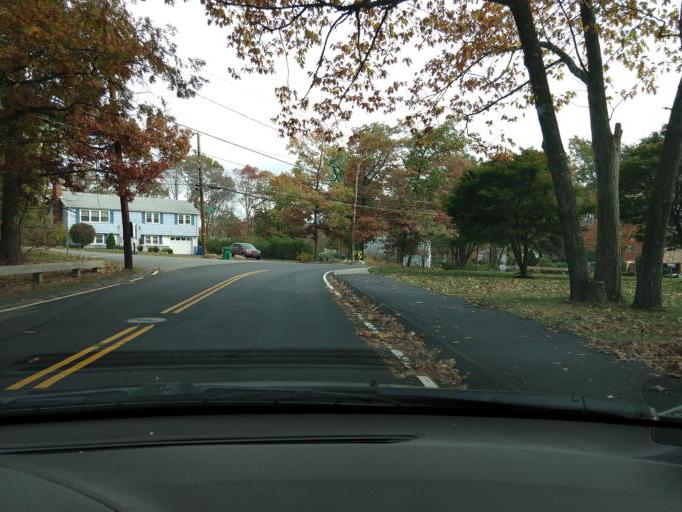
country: US
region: Massachusetts
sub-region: Middlesex County
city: Burlington
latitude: 42.5180
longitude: -71.1948
